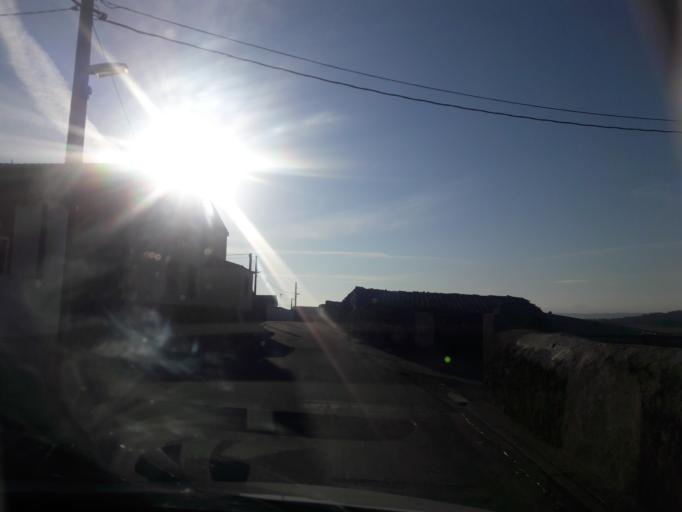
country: ES
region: Castille and Leon
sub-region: Provincia de Salamanca
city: Montejo
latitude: 40.6313
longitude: -5.6220
